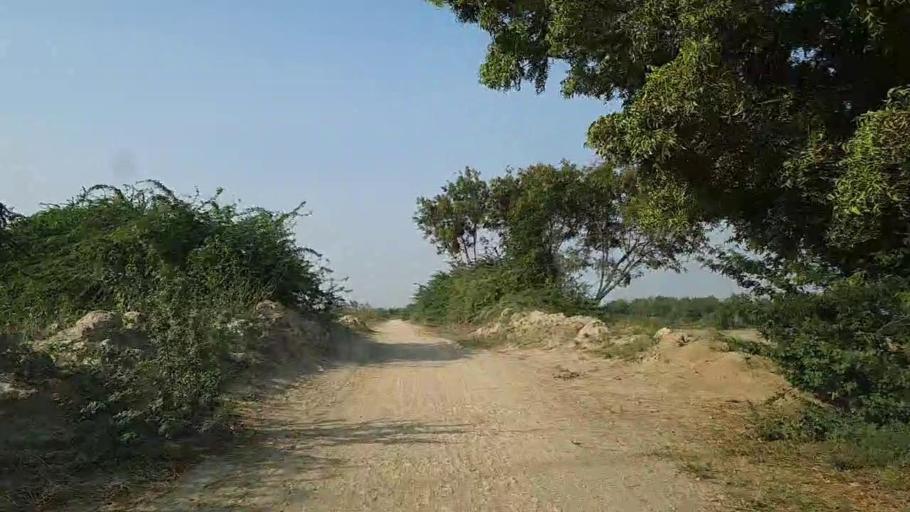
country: PK
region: Sindh
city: Mirpur Sakro
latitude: 24.5923
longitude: 67.6490
